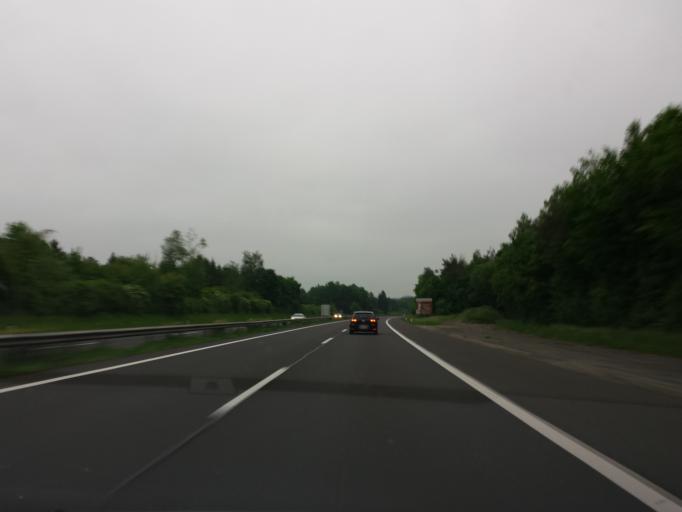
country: AT
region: Styria
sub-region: Politischer Bezirk Hartberg-Fuerstenfeld
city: Hainersdorf
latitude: 47.1037
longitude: 15.9847
